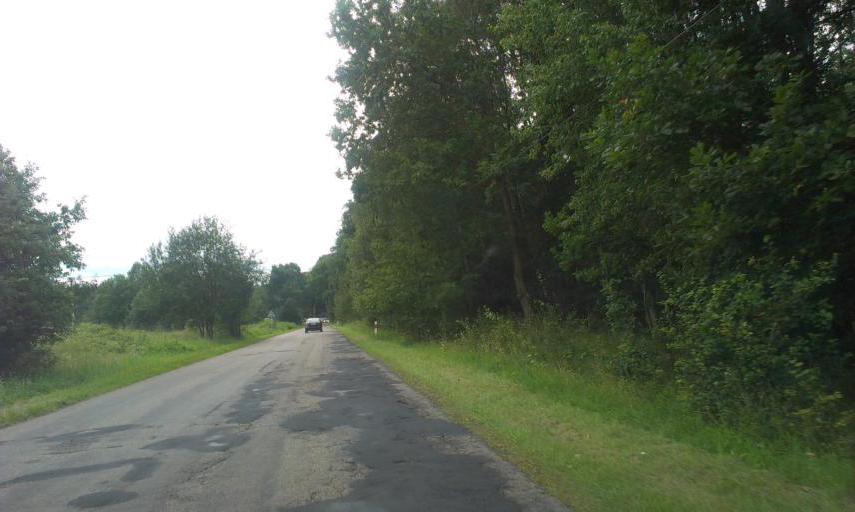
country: PL
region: West Pomeranian Voivodeship
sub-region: Powiat szczecinecki
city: Barwice
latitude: 53.6767
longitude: 16.3412
